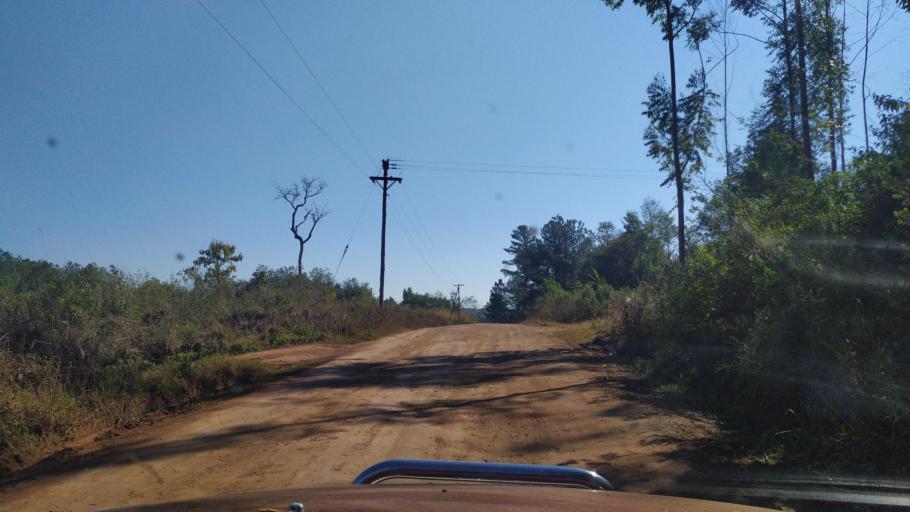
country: AR
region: Misiones
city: El Alcazar
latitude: -26.7183
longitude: -54.6923
